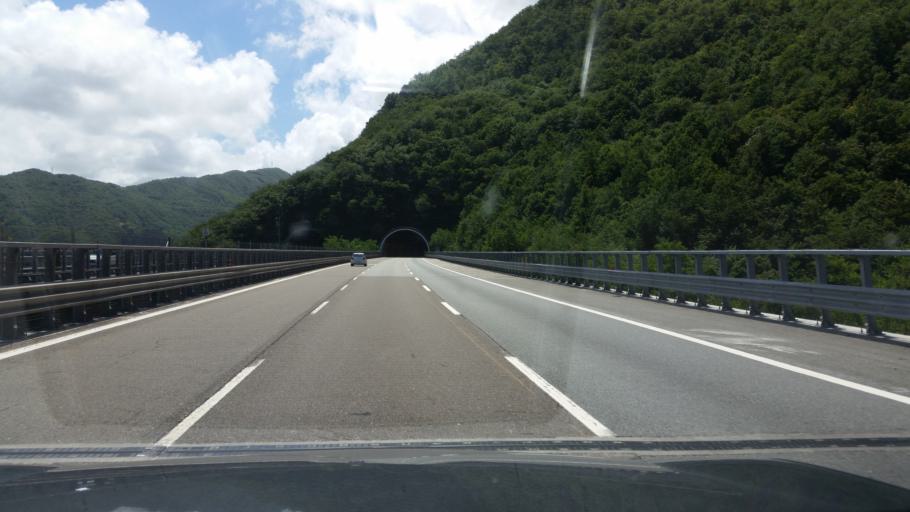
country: IT
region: Liguria
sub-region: Provincia di Genova
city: Rossiglione
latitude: 44.5541
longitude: 8.6696
